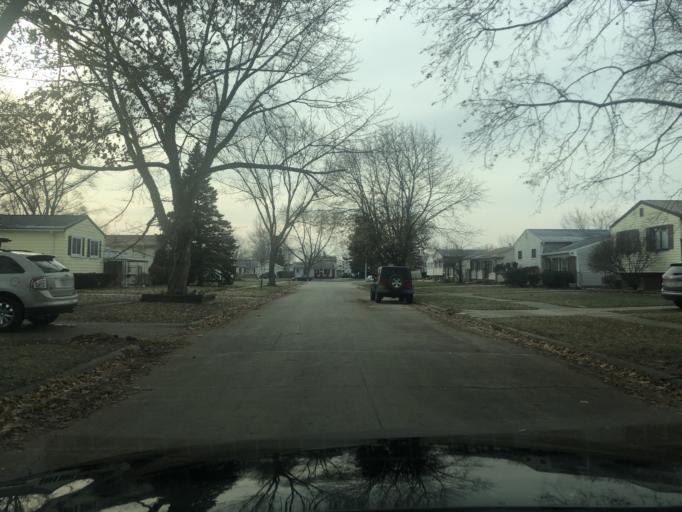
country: US
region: Michigan
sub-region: Wayne County
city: Taylor
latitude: 42.1899
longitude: -83.3203
